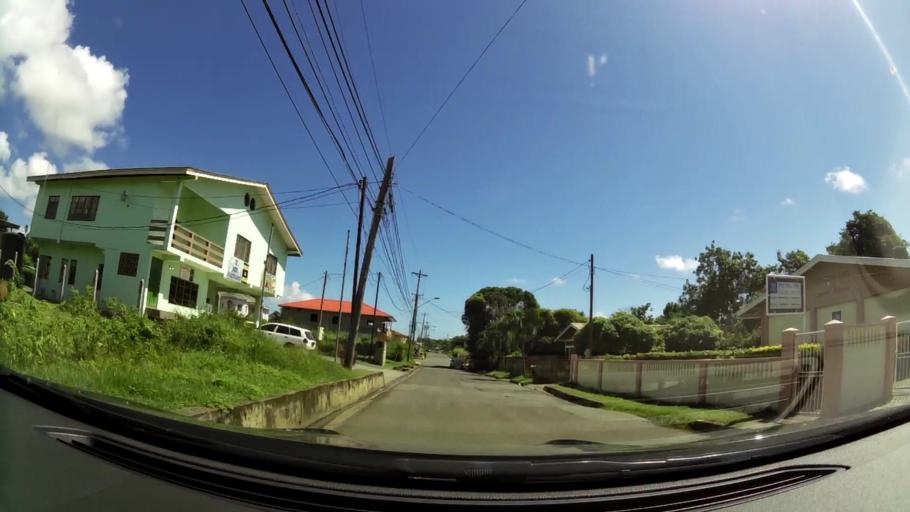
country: TT
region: Tobago
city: Scarborough
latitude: 11.1694
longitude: -60.7931
